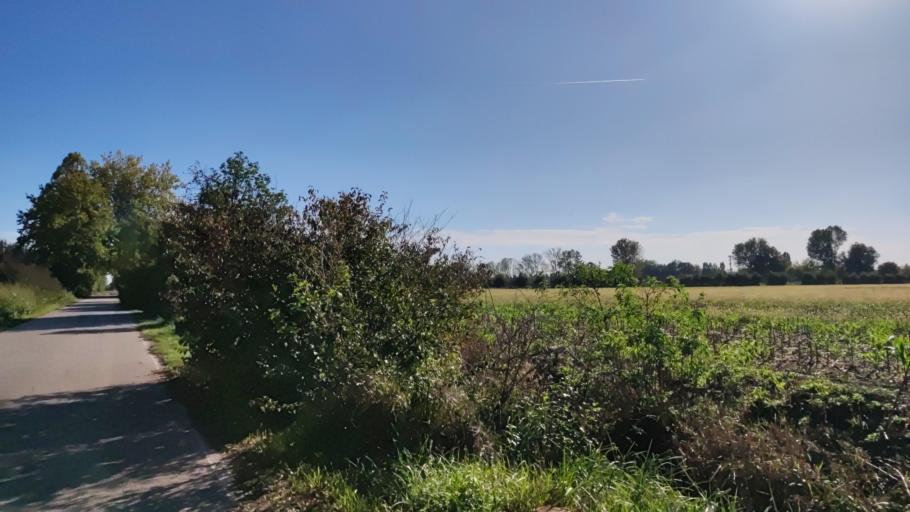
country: IT
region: Lombardy
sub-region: Citta metropolitana di Milano
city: Vigliano-Bettolino
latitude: 45.4358
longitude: 9.3312
